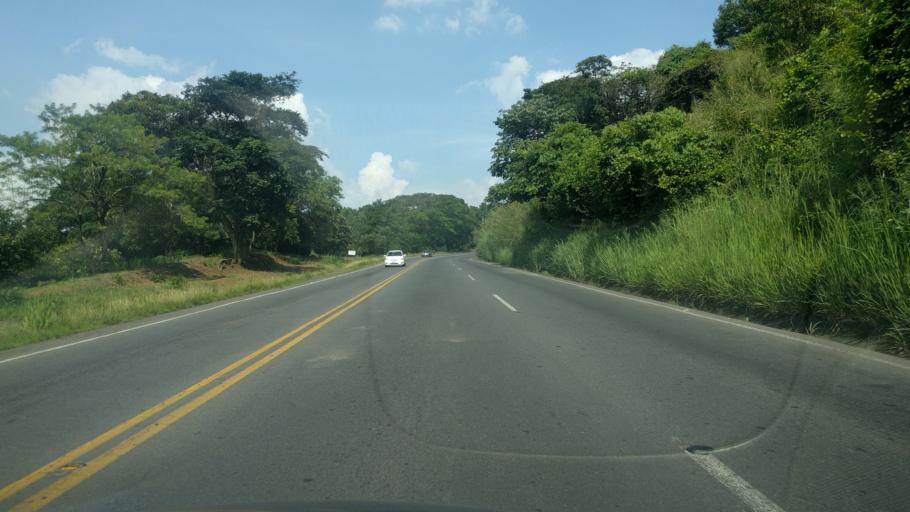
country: CR
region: Alajuela
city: Carrillos
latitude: 10.0179
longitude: -84.3323
